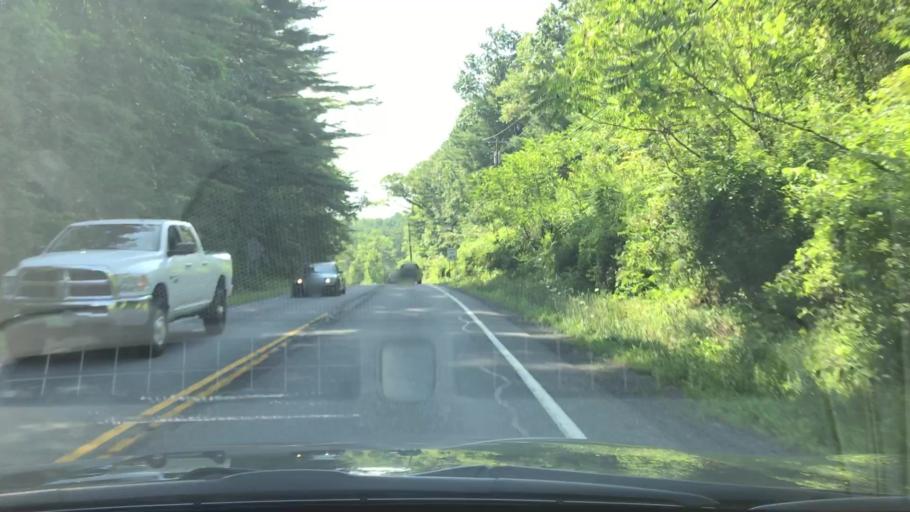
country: US
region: New York
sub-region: Warren County
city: Queensbury
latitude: 43.4080
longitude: -73.5553
